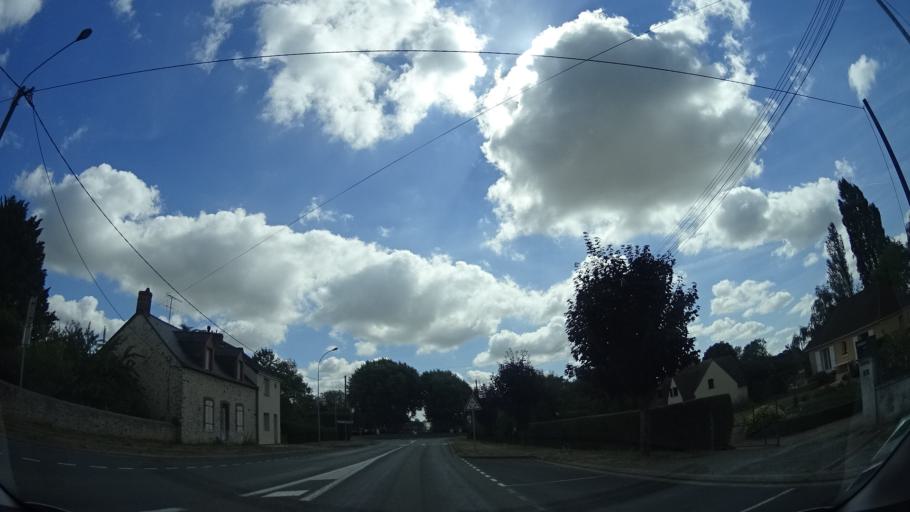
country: FR
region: Pays de la Loire
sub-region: Departement de la Mayenne
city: Meslay-du-Maine
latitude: 47.9488
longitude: -0.5436
